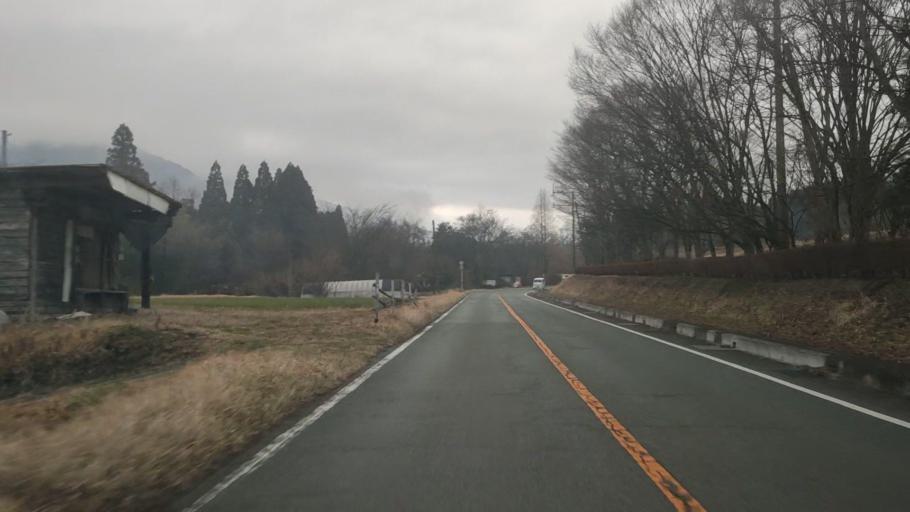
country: JP
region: Kumamoto
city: Aso
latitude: 32.8484
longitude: 131.1491
